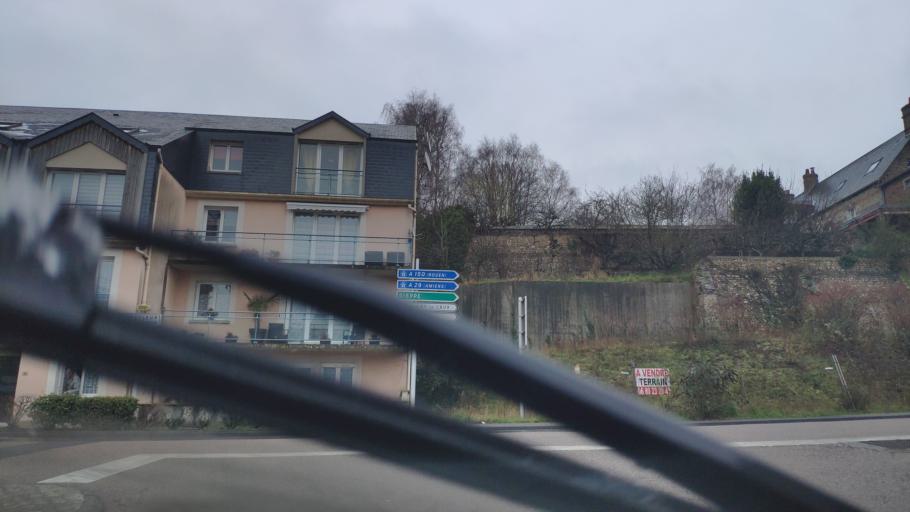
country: FR
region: Haute-Normandie
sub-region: Departement de la Seine-Maritime
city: Cany-Barville
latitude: 49.7882
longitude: 0.6387
